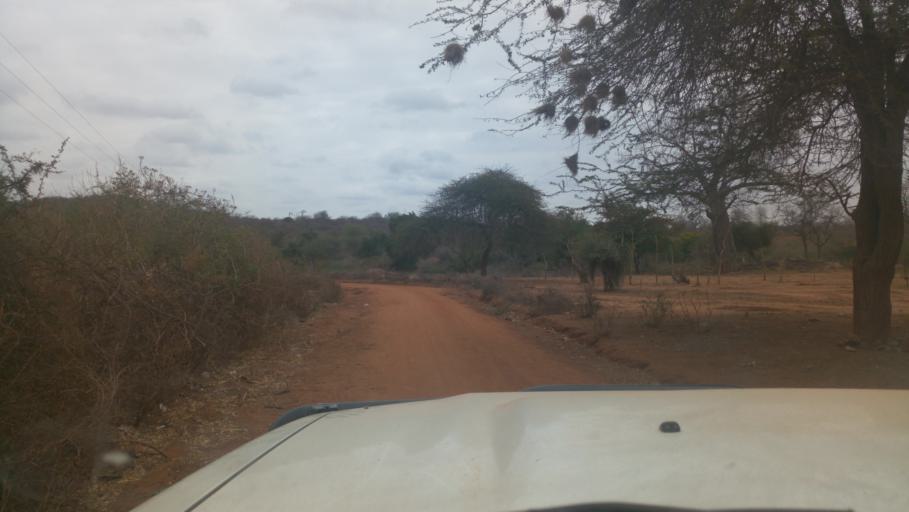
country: KE
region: Makueni
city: Makueni
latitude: -1.9757
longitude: 38.0617
